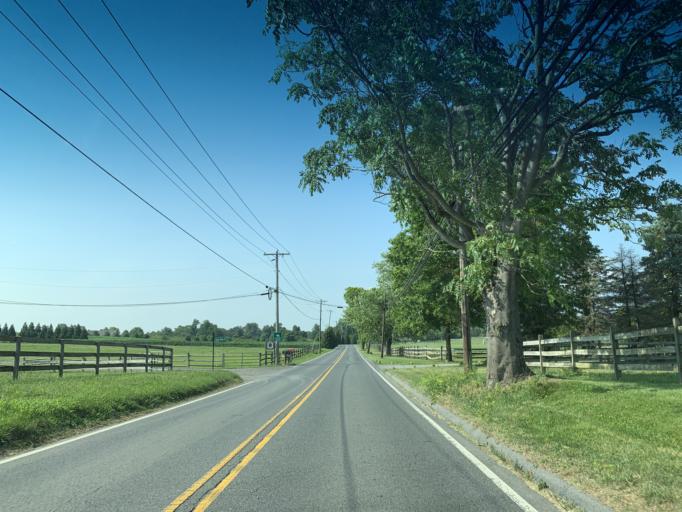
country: US
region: Maryland
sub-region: Montgomery County
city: Poolesville
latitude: 39.1592
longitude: -77.4189
